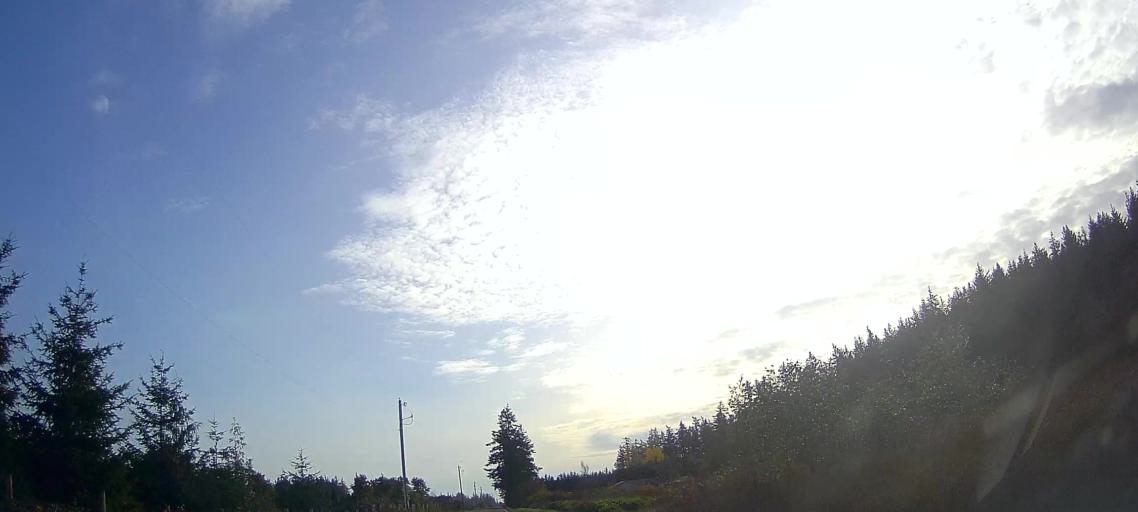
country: US
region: Washington
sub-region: Snohomish County
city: Stanwood
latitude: 48.2487
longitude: -122.4170
